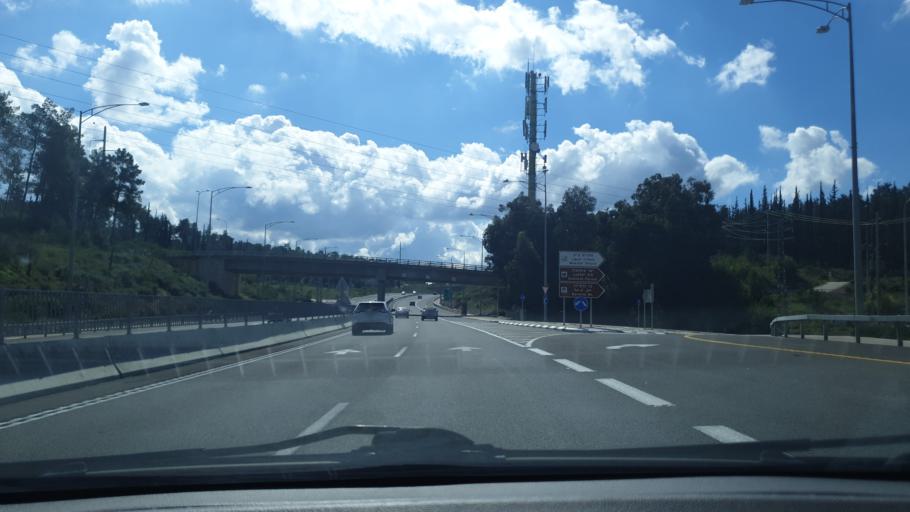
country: IL
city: Mevo horon
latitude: 31.7994
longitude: 35.0143
